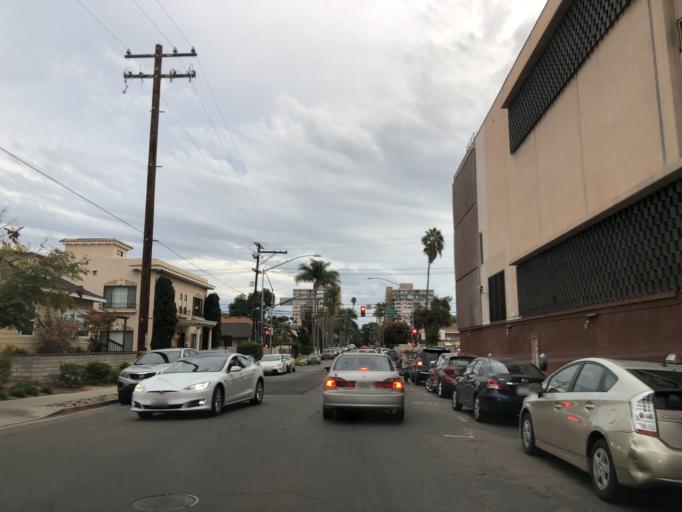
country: US
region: California
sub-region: San Diego County
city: San Diego
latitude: 32.7476
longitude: -117.1584
